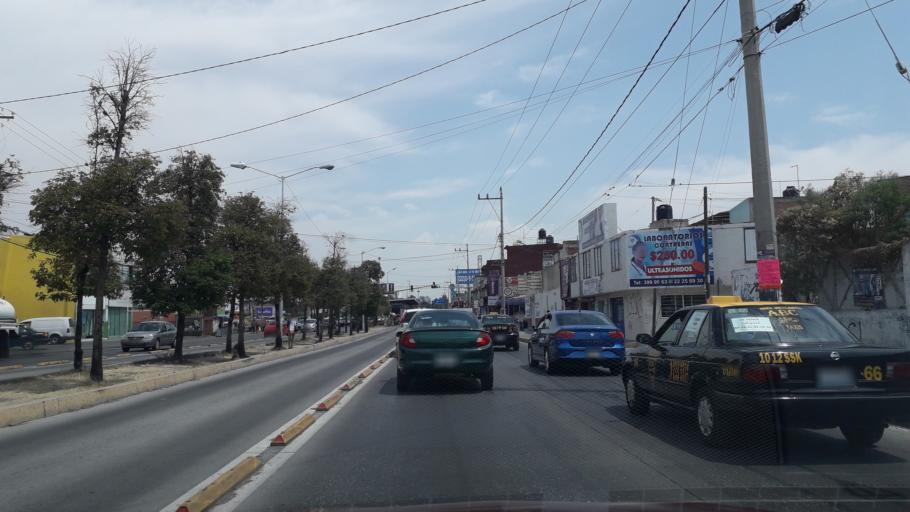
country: MX
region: Puebla
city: Tlazcalancingo
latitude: 19.0023
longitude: -98.2392
